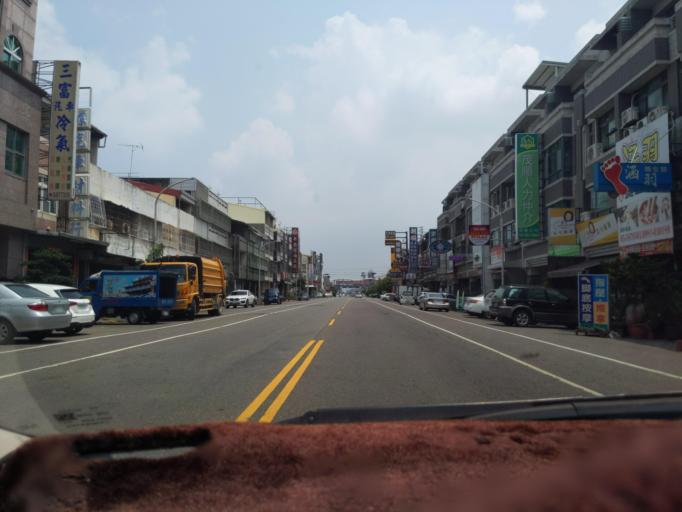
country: TW
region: Taiwan
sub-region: Yunlin
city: Douliu
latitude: 23.7976
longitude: 120.4666
